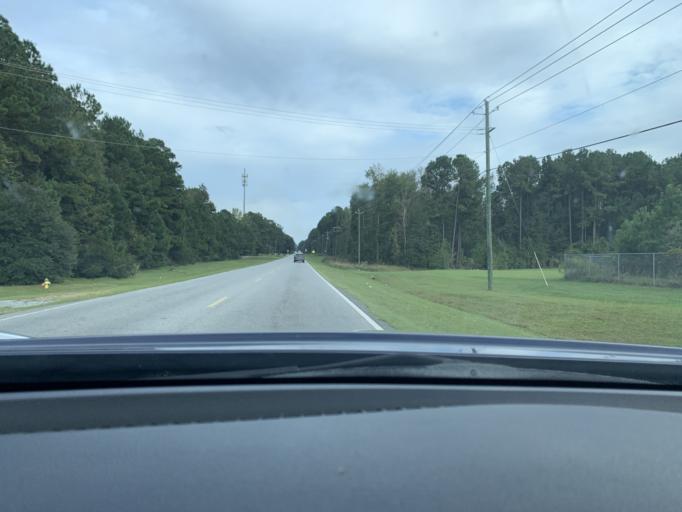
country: US
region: Georgia
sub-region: Chatham County
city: Pooler
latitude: 32.0962
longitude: -81.2697
